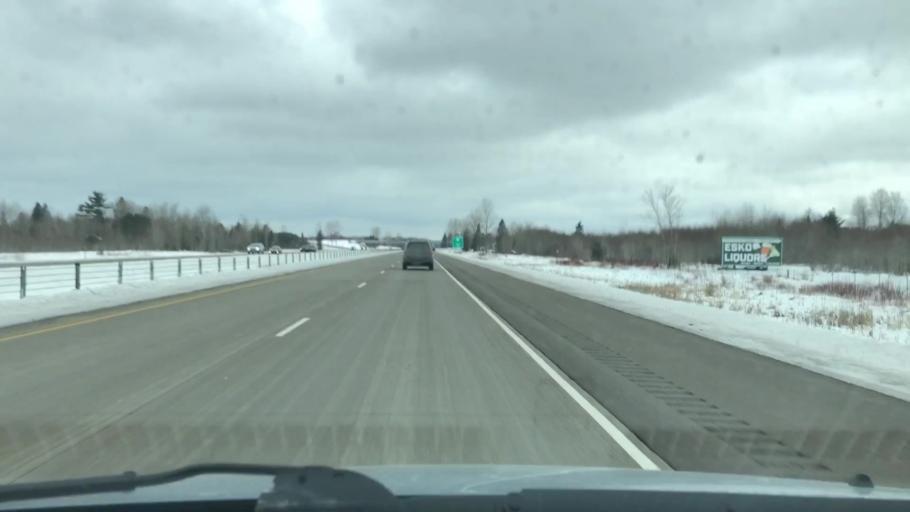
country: US
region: Minnesota
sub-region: Carlton County
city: Esko
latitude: 46.6971
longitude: -92.3553
